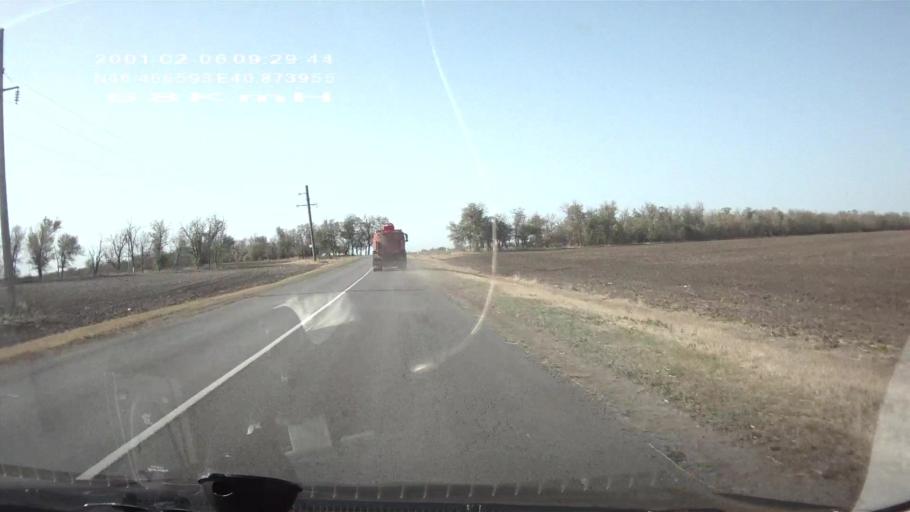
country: RU
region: Rostov
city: Tselina
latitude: 46.4662
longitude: 40.8735
